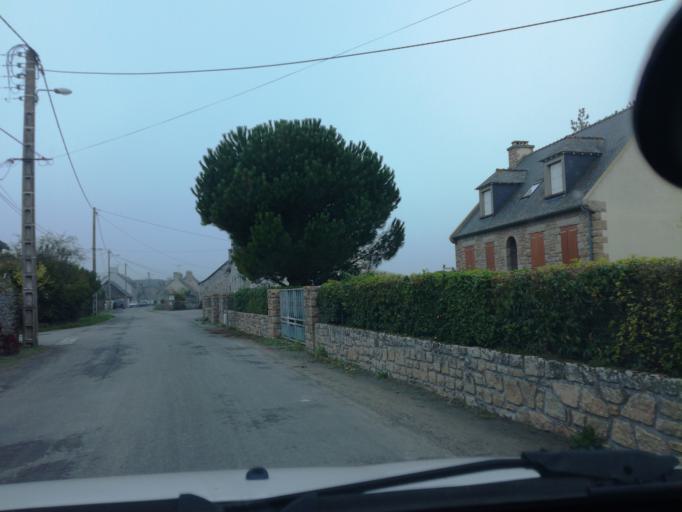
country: FR
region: Brittany
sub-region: Departement d'Ille-et-Vilaine
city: Cherrueix
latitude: 48.6061
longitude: -1.7134
